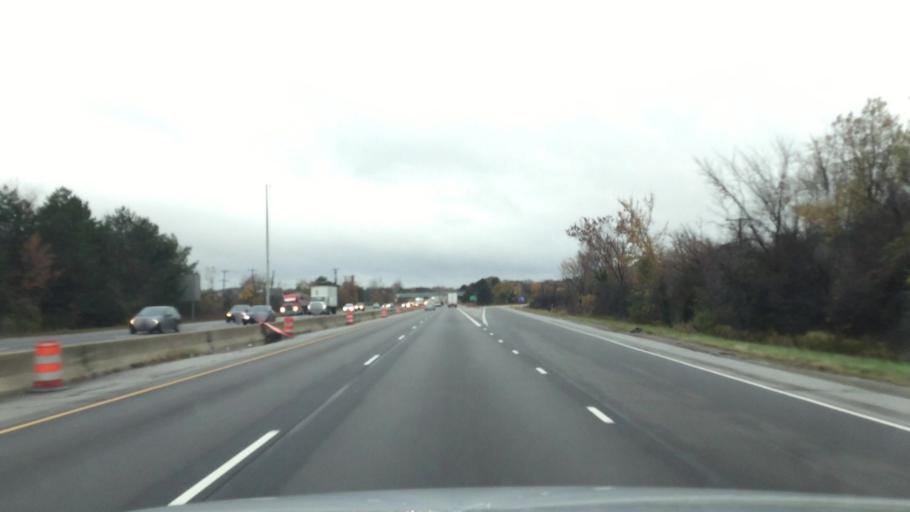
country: US
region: Michigan
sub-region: Washtenaw County
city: Ann Arbor
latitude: 42.2407
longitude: -83.7568
